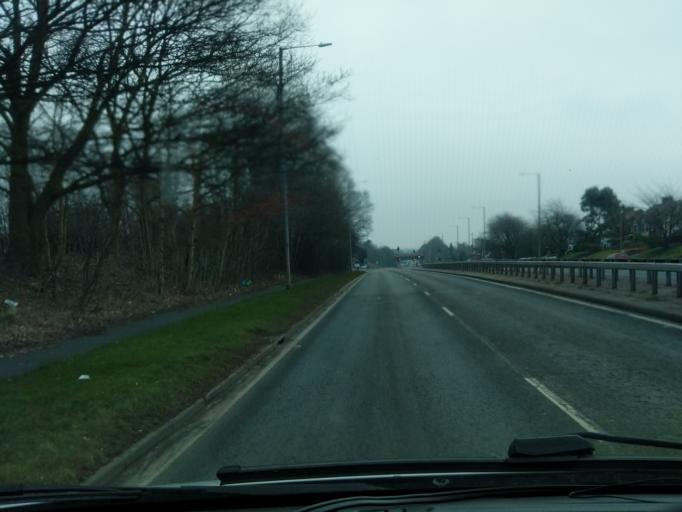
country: GB
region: England
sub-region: St. Helens
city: St Helens
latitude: 53.4726
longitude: -2.7224
